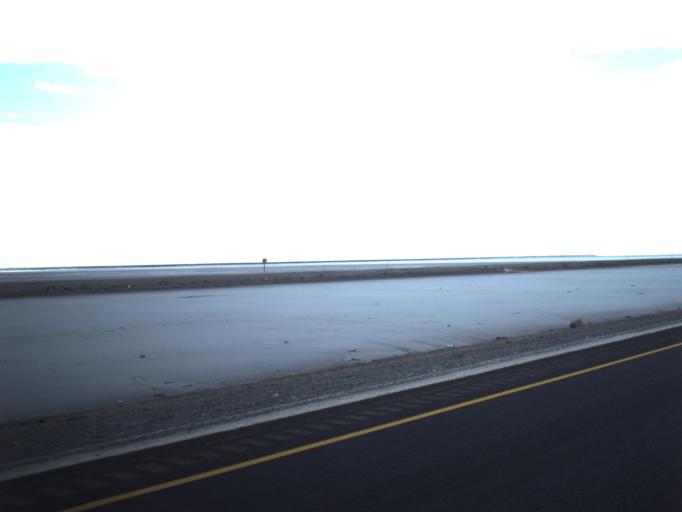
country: US
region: Utah
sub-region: Tooele County
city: Wendover
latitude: 40.7320
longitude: -113.5471
